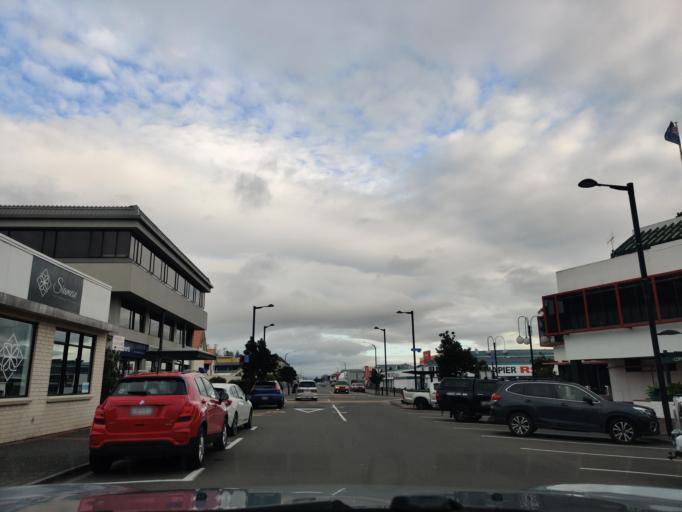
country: NZ
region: Hawke's Bay
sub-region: Napier City
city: Napier
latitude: -39.4935
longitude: 176.9182
